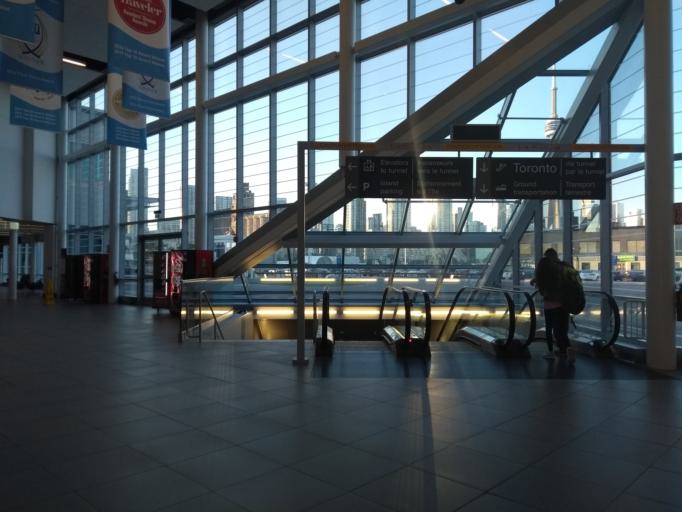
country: CA
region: Ontario
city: Toronto
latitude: 43.6318
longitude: -79.3961
